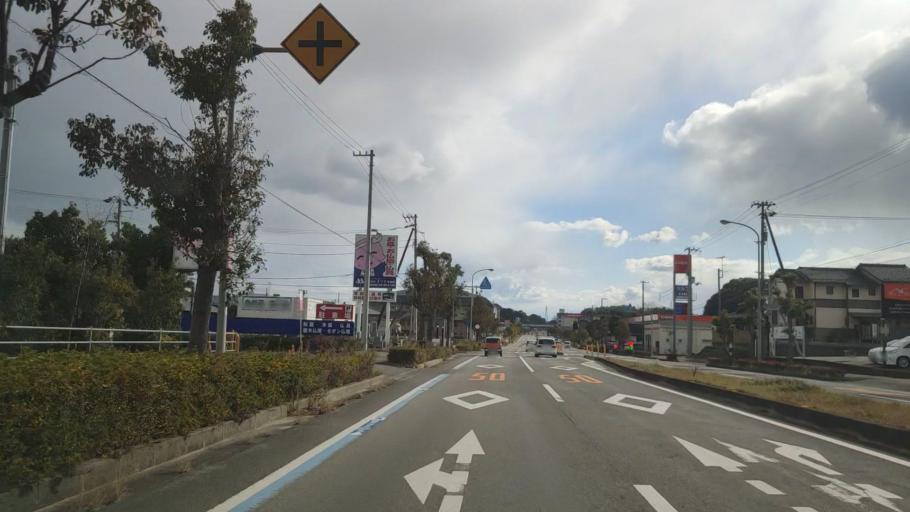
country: JP
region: Ehime
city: Hojo
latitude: 34.0607
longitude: 132.9652
